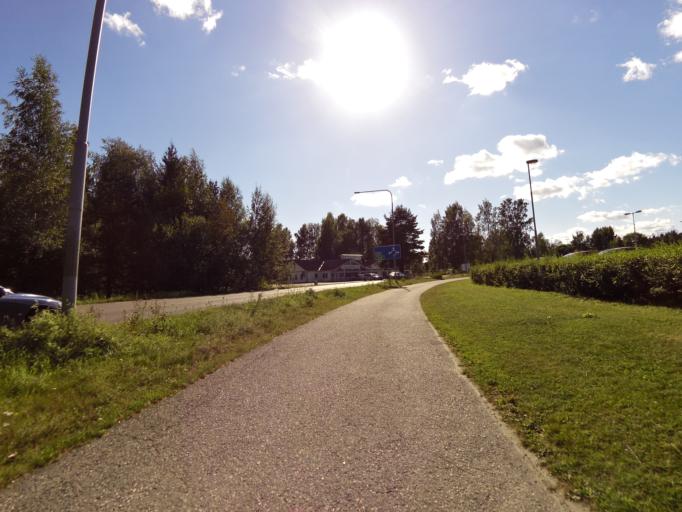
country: SE
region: Gaevleborg
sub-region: Gavle Kommun
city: Gavle
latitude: 60.6935
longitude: 17.1511
